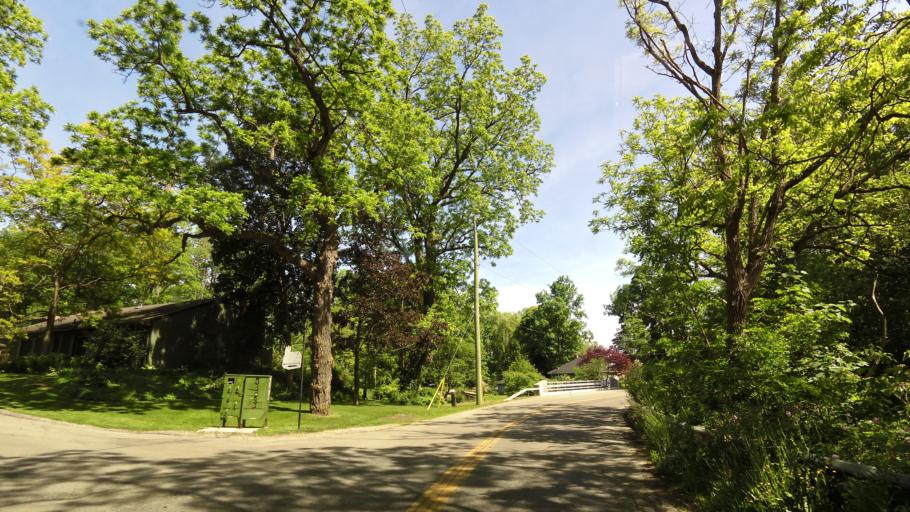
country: CA
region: Ontario
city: Norfolk County
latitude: 42.7553
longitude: -80.2576
